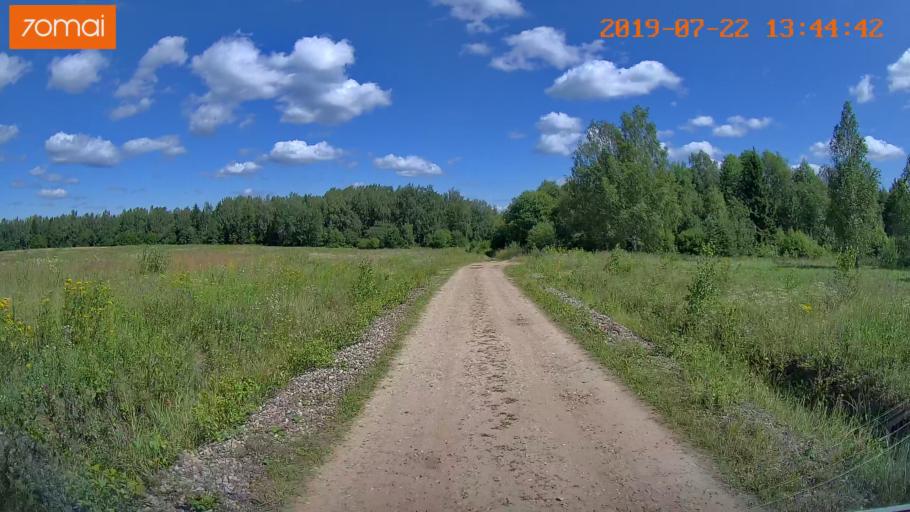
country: RU
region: Ivanovo
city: Novo-Talitsy
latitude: 57.0851
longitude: 40.8777
